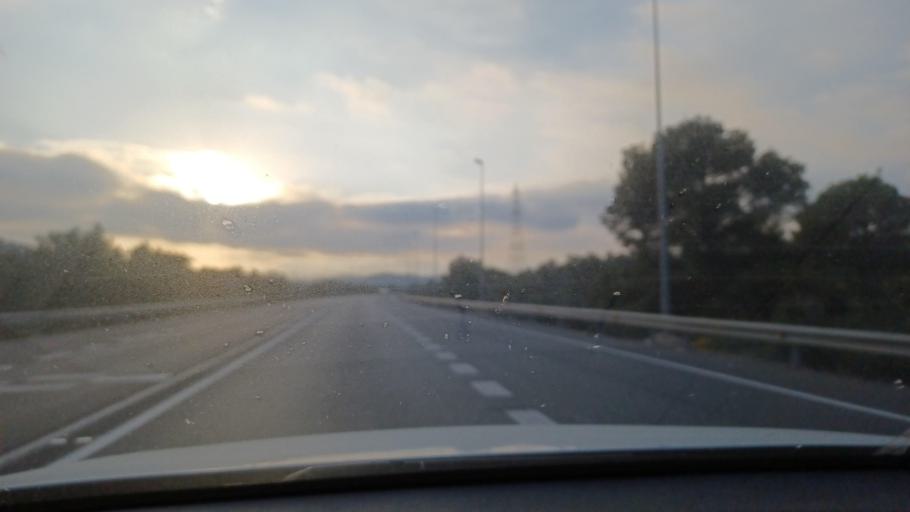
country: ES
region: Catalonia
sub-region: Provincia de Tarragona
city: El Perello
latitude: 40.8968
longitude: 0.7471
